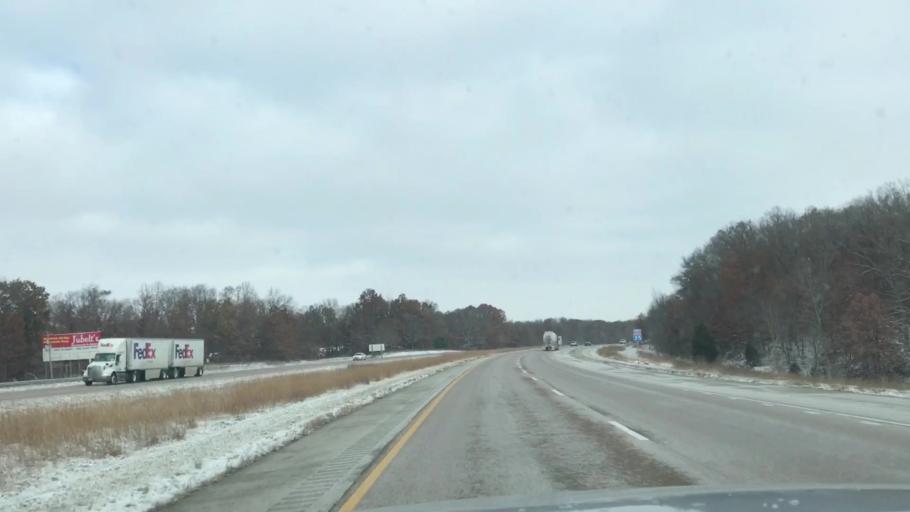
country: US
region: Illinois
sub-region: Macoupin County
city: Mount Olive
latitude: 39.0779
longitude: -89.7555
